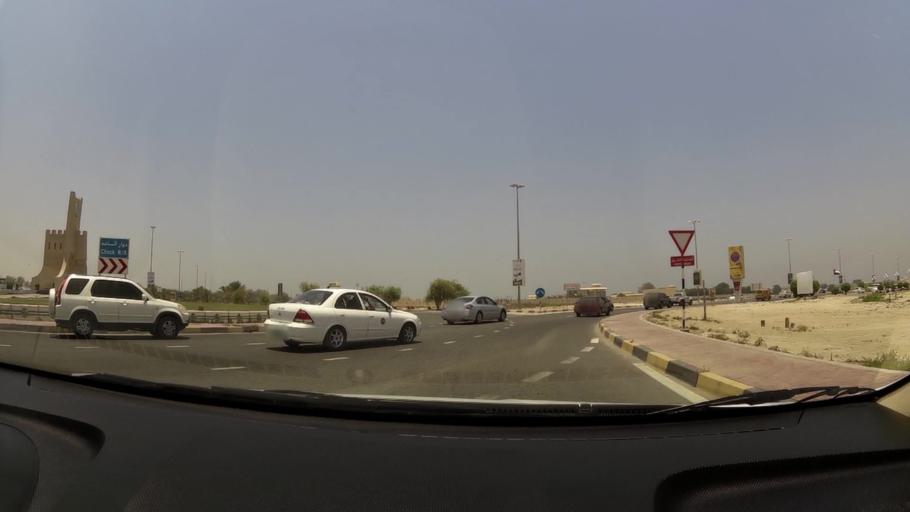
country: AE
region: Umm al Qaywayn
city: Umm al Qaywayn
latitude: 25.5304
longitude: 55.5387
